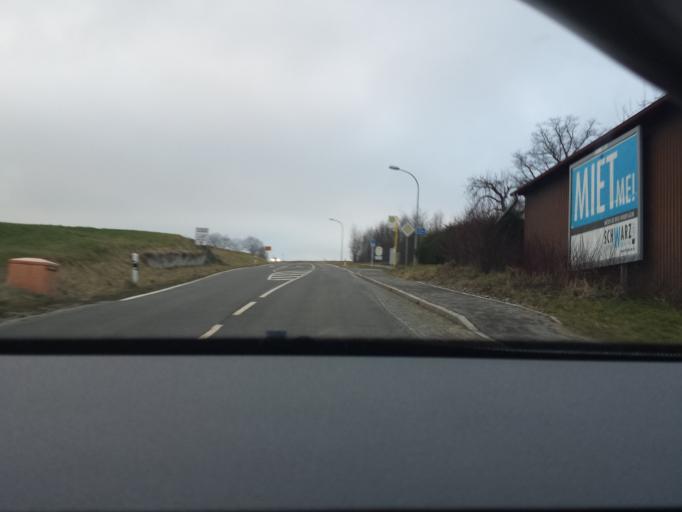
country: DE
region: Baden-Wuerttemberg
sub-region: Tuebingen Region
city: Maselheim
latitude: 48.1207
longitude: 9.8610
